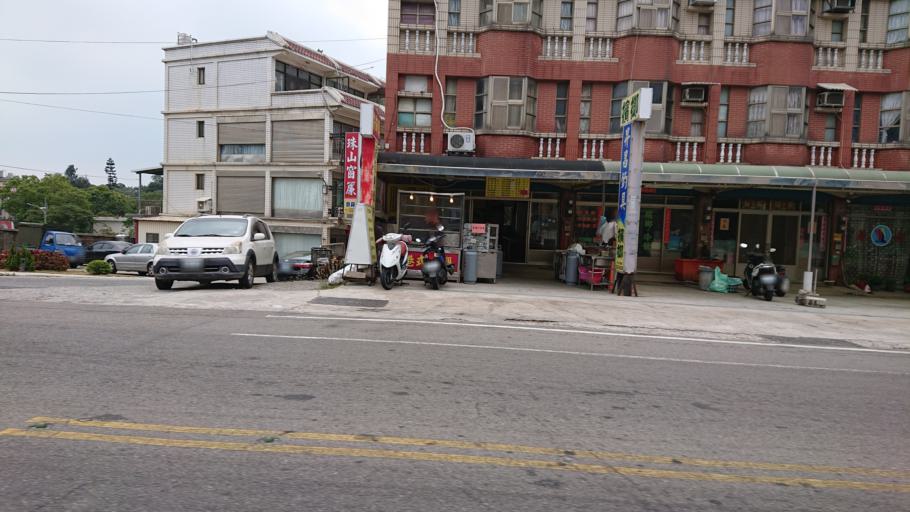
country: TW
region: Fukien
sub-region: Kinmen
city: Jincheng
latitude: 24.4369
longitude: 118.4083
